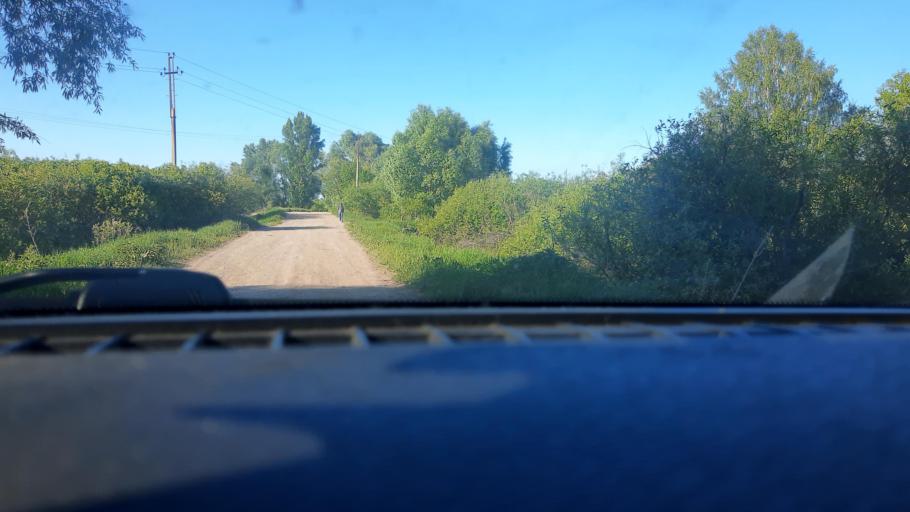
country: RU
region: Bashkortostan
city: Ulukulevo
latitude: 54.5549
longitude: 56.3243
